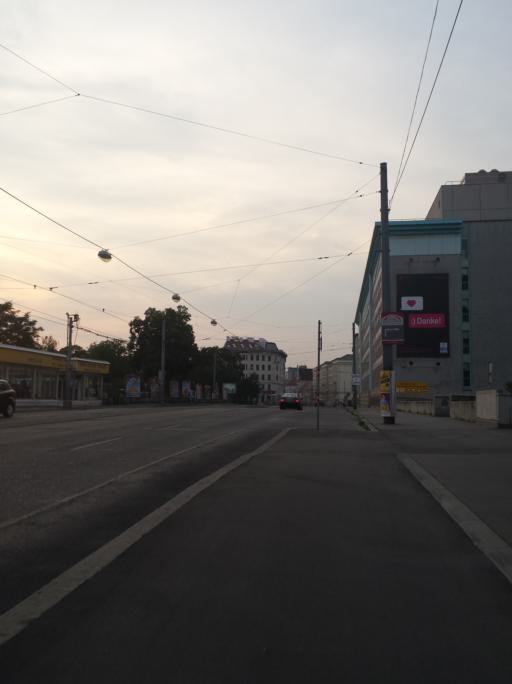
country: AT
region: Vienna
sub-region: Wien Stadt
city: Vienna
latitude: 48.1872
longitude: 16.4018
